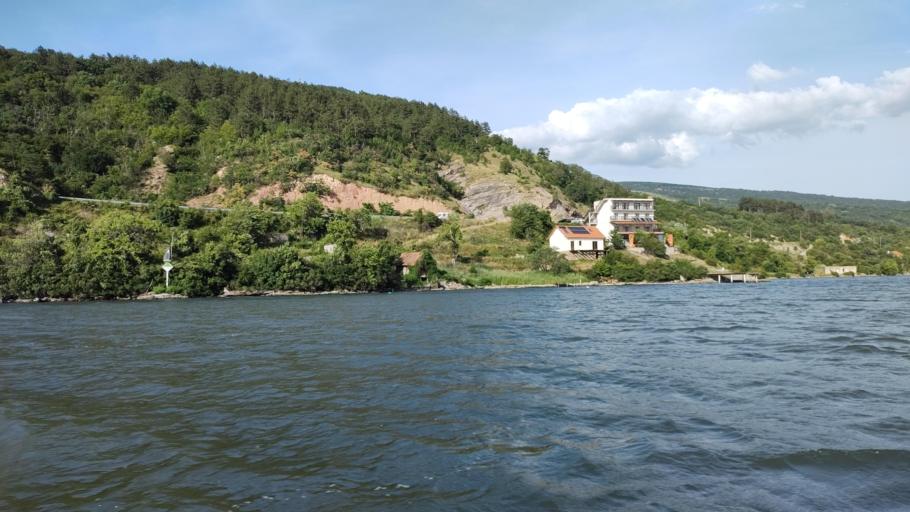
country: RO
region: Mehedinti
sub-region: Comuna Svinita
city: Svinita
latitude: 44.5015
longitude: 22.0865
